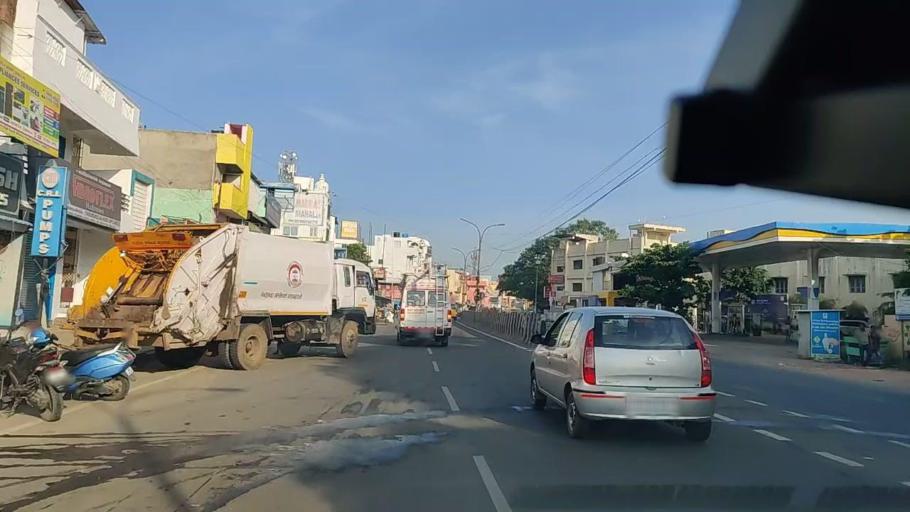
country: IN
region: Tamil Nadu
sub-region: Chennai
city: George Town
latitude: 13.1194
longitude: 80.2560
